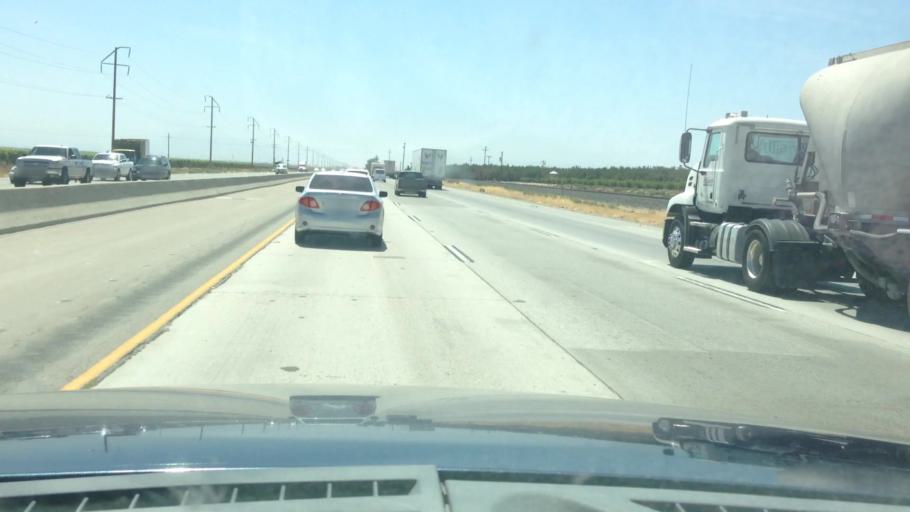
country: US
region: California
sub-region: Kern County
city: Rosedale
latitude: 35.4807
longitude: -119.1397
